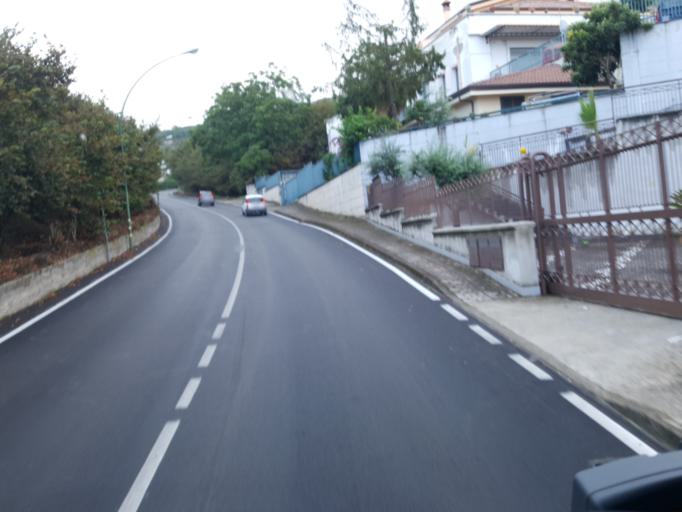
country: IT
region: Campania
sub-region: Provincia di Napoli
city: Carbonara di Nola
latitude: 40.8788
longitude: 14.5811
